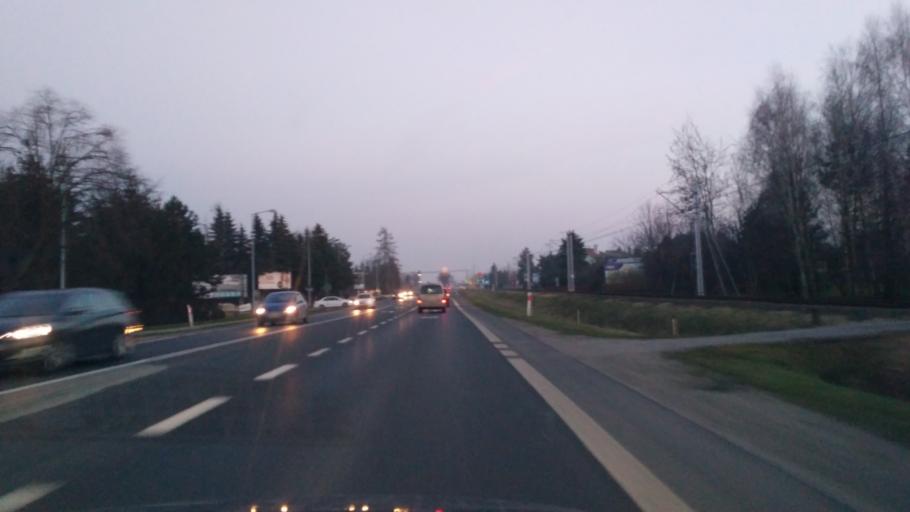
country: PL
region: Subcarpathian Voivodeship
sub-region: Powiat rzeszowski
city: Rudna Mala
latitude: 50.0788
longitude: 21.9862
